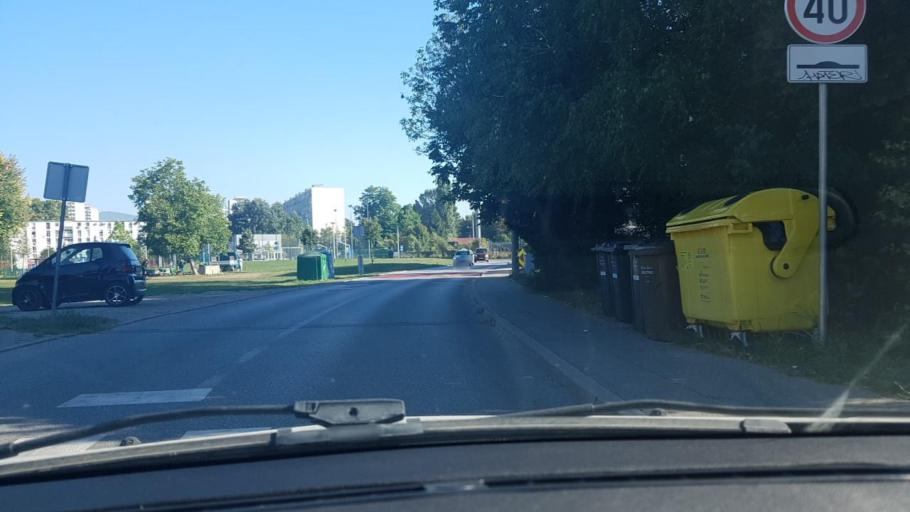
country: HR
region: Grad Zagreb
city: Novi Zagreb
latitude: 45.7697
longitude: 15.9698
